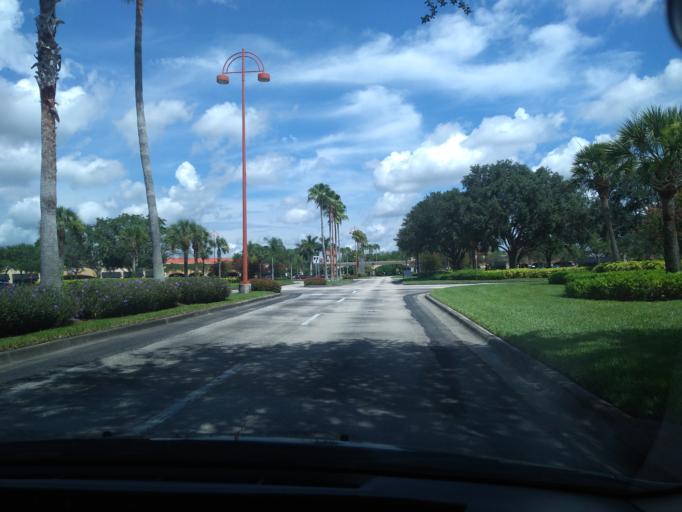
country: US
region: Florida
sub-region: Indian River County
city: West Vero Corridor
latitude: 27.6351
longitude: -80.5209
